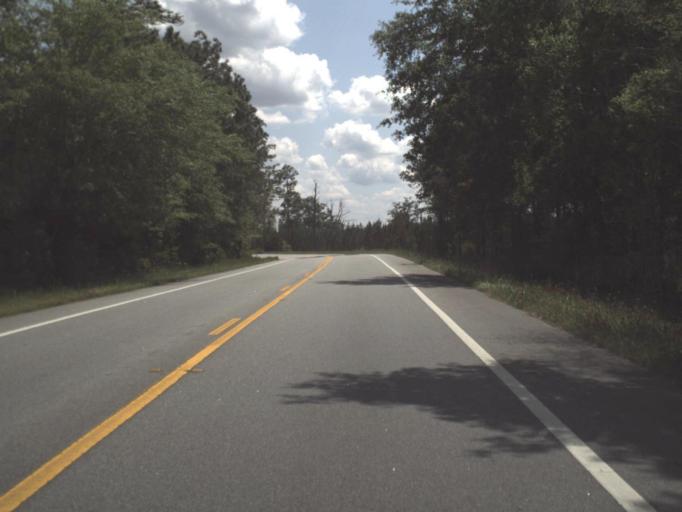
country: US
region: Alabama
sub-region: Escambia County
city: Atmore
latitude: 30.8602
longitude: -87.4425
